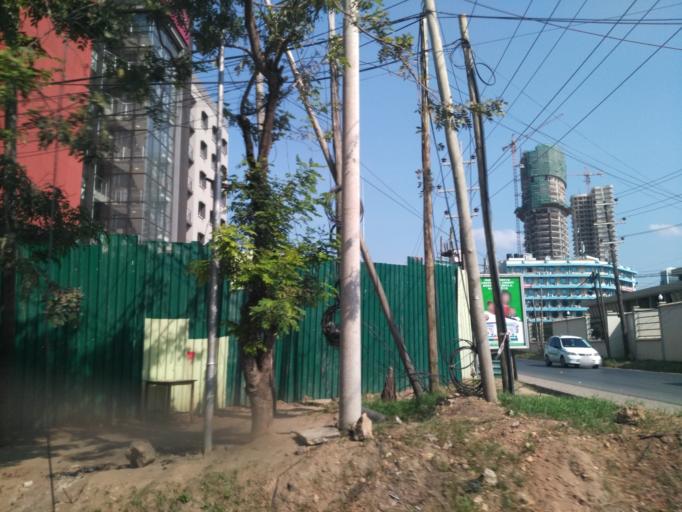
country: TZ
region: Dar es Salaam
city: Dar es Salaam
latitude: -6.8103
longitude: 39.2850
